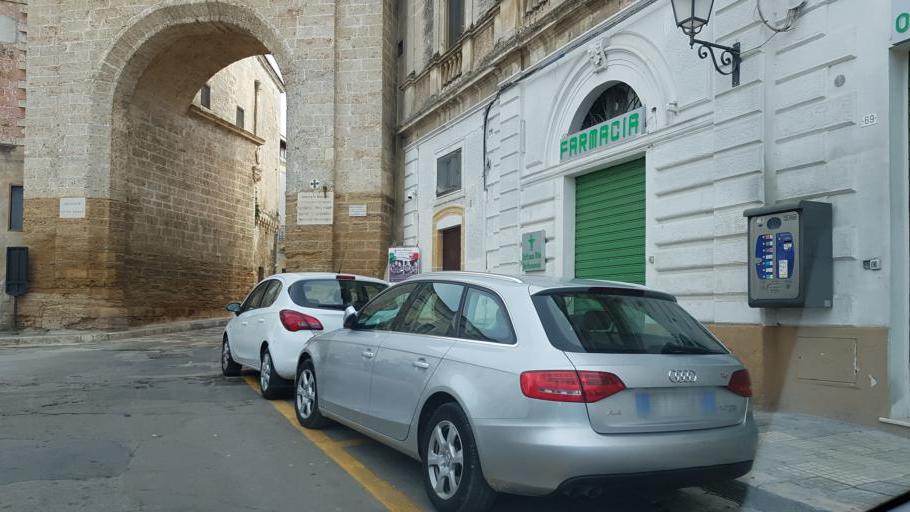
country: IT
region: Apulia
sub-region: Provincia di Brindisi
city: Mesagne
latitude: 40.5606
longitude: 17.8082
